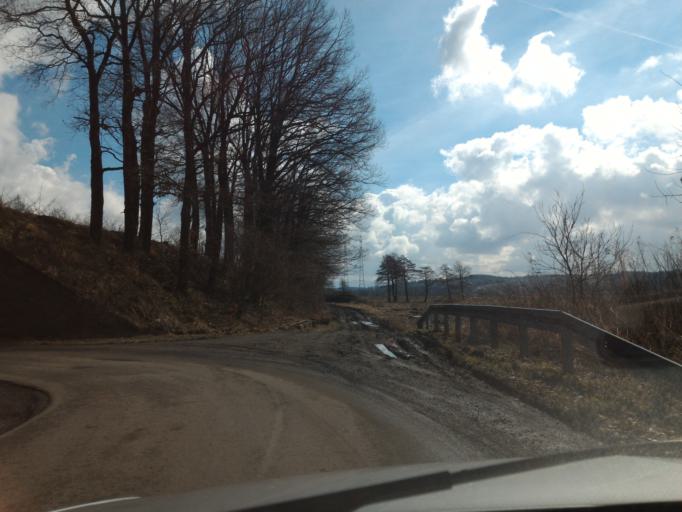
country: PL
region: Silesian Voivodeship
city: Zawidow
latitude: 51.0353
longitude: 15.0192
